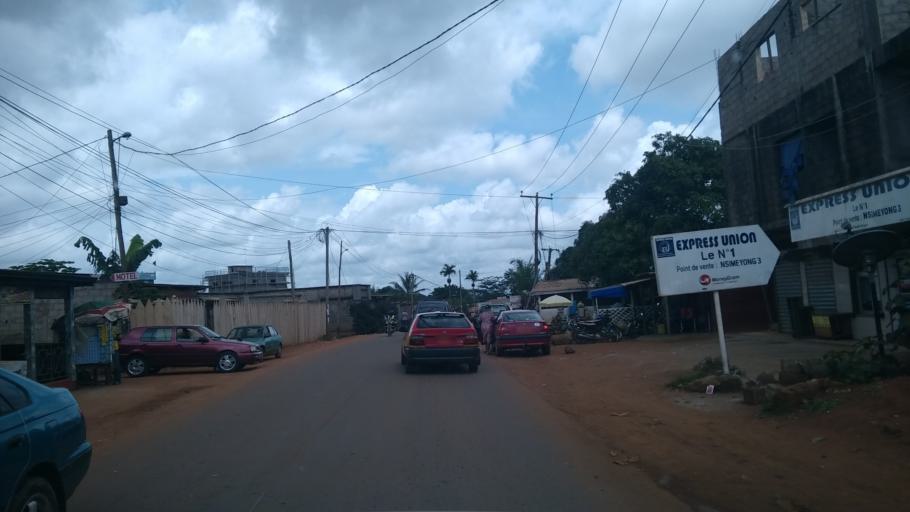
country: CM
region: Centre
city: Yaounde
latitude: 3.8122
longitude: 11.4900
